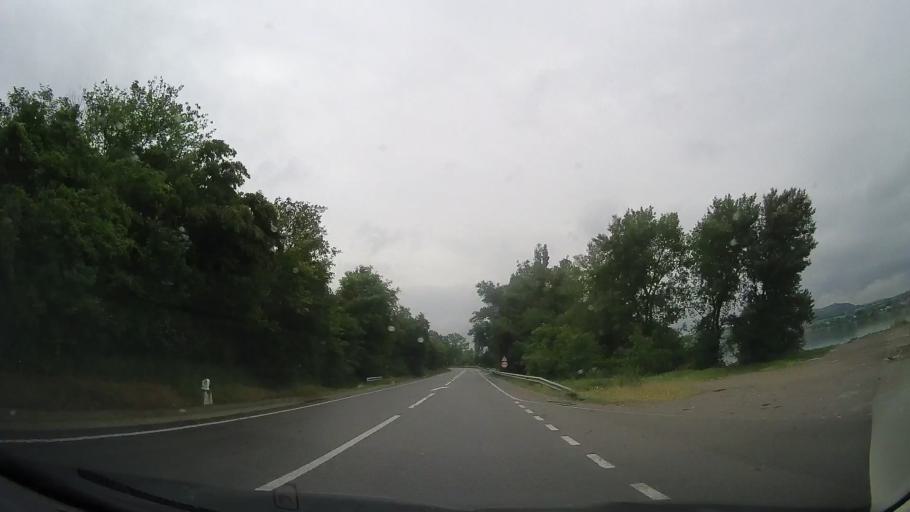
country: RO
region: Mehedinti
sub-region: Municipiul Drobeta-Turnu Severin
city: Gura Vaii
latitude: 44.6500
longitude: 22.5683
